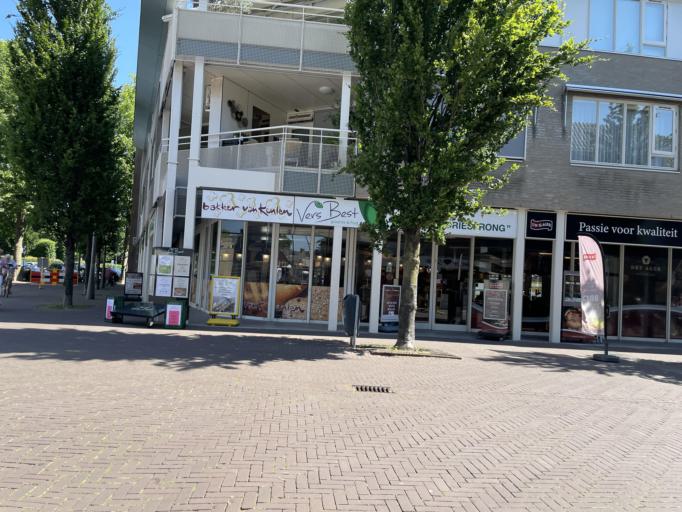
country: NL
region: North Brabant
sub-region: Gemeente 's-Hertogenbosch
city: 's-Hertogenbosch
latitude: 51.7175
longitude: 5.3634
